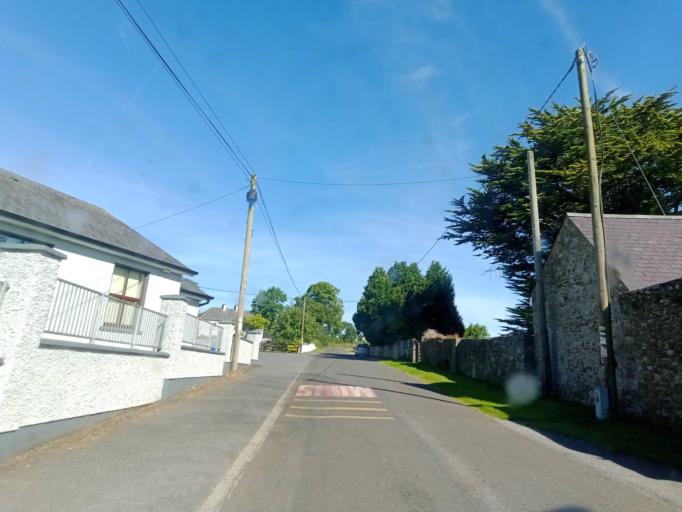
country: IE
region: Leinster
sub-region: Kilkenny
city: Ballyragget
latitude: 52.7574
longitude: -7.4037
